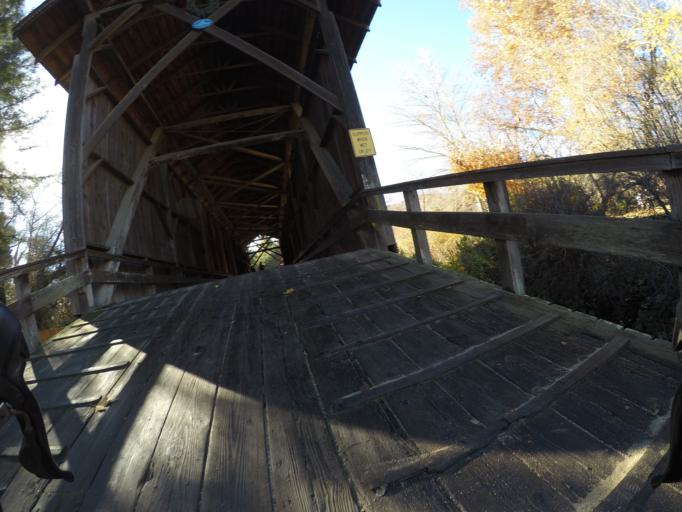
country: US
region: California
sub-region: Santa Cruz County
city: Felton
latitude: 37.0509
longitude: -122.0706
